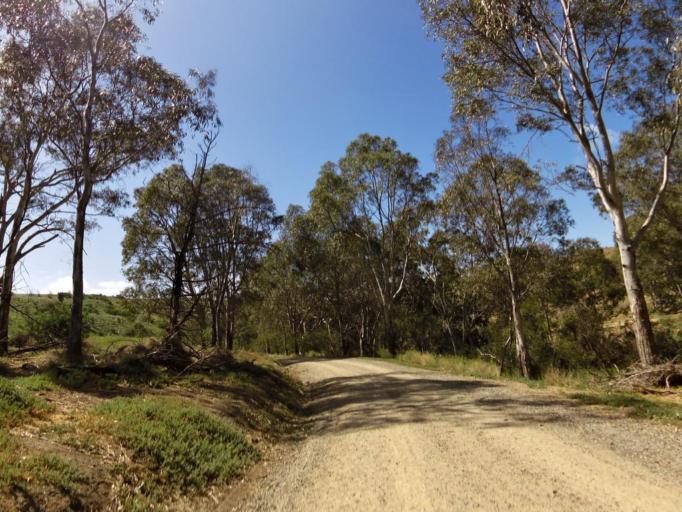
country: AU
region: Victoria
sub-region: Brimbank
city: Kealba
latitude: -37.7414
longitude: 144.8342
